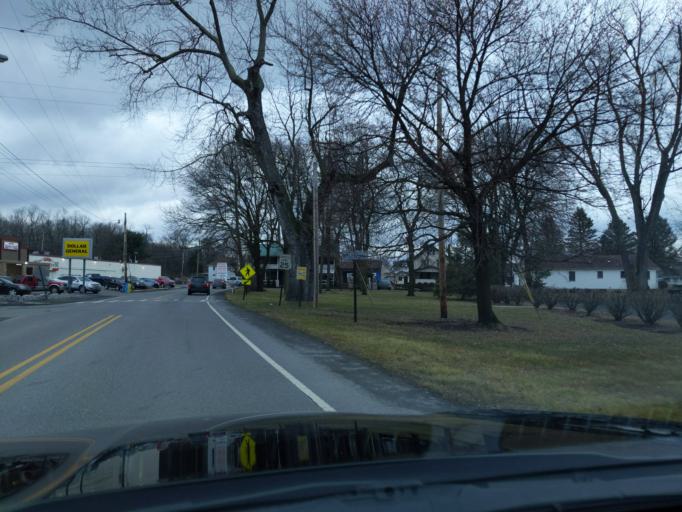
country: US
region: Pennsylvania
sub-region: Blair County
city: Bellwood
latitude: 40.5947
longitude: -78.3362
